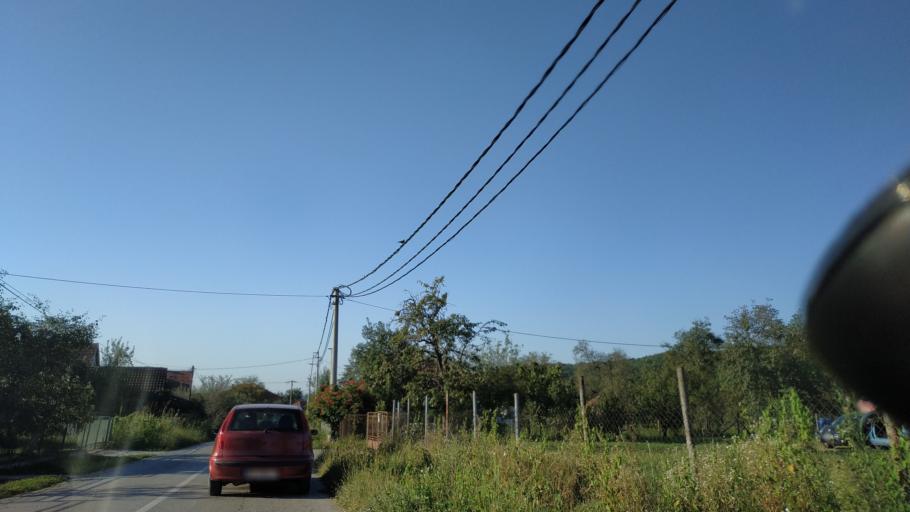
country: RS
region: Central Serbia
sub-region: Rasinski Okrug
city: Krusevac
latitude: 43.4937
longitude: 21.3427
